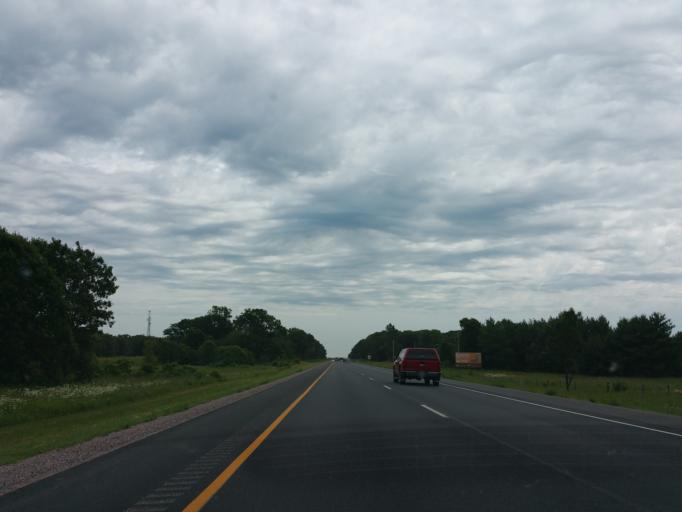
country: US
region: Wisconsin
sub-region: Juneau County
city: Mauston
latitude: 43.7541
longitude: -89.9587
